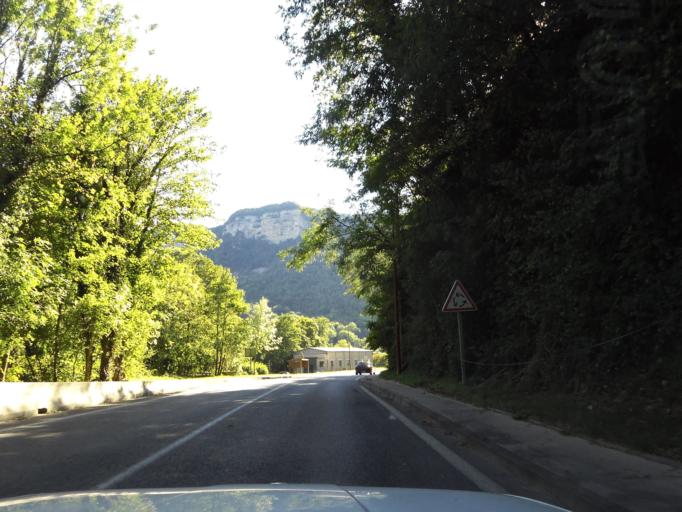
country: FR
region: Rhone-Alpes
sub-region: Departement de l'Ain
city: Saint-Rambert-en-Bugey
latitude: 45.9370
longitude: 5.4265
